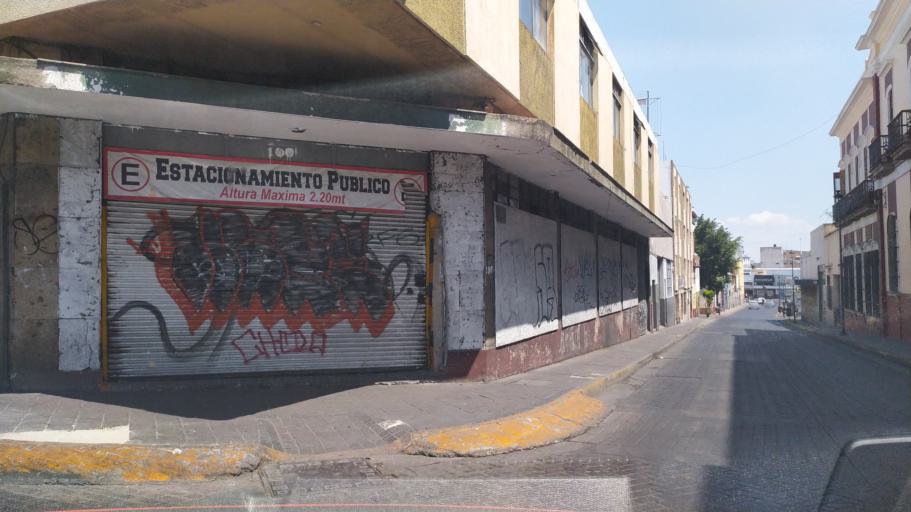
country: MX
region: Jalisco
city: Guadalajara
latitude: 20.6729
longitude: -103.3452
